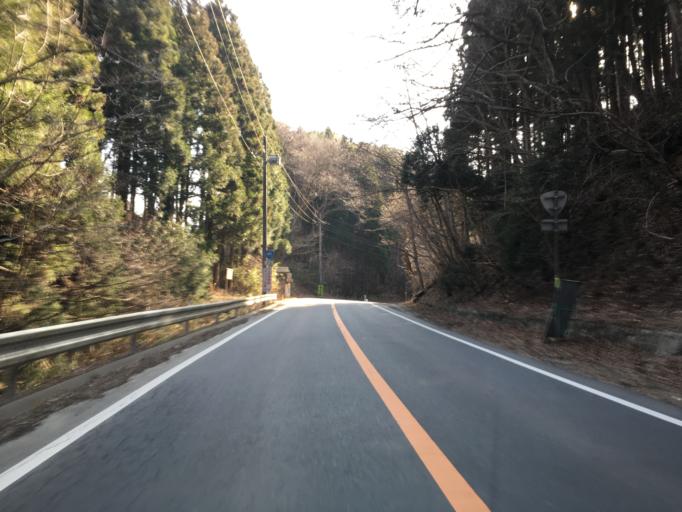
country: JP
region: Ibaraki
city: Takahagi
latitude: 36.7394
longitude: 140.5601
